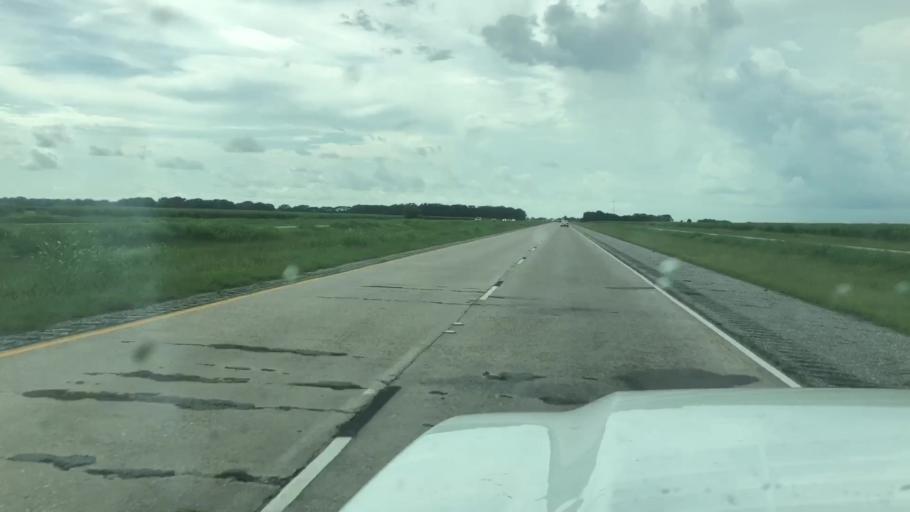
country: US
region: Louisiana
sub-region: Saint Mary Parish
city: Baldwin
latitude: 29.8511
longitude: -91.5982
